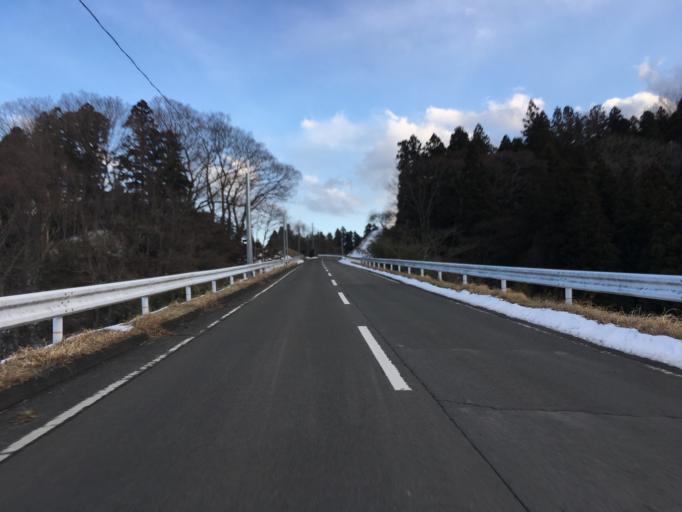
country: JP
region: Fukushima
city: Fukushima-shi
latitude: 37.6445
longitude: 140.5853
